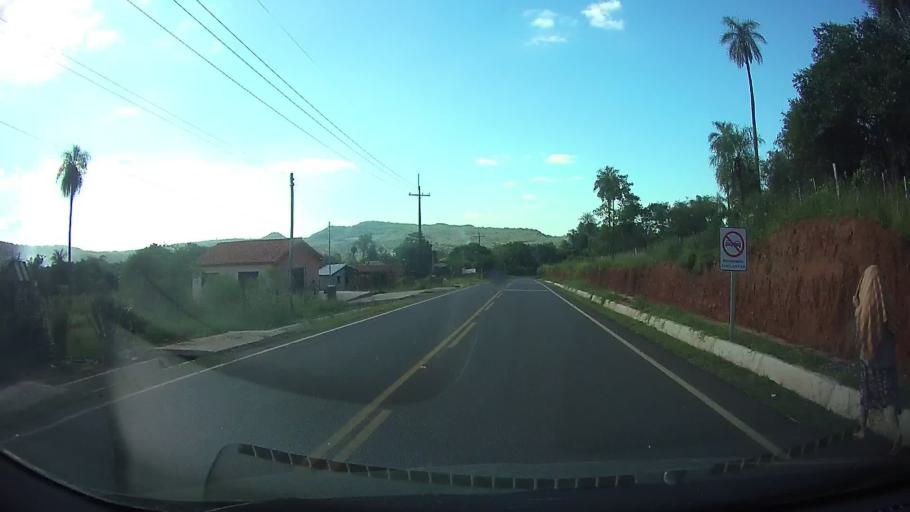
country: PY
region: Cordillera
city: Caacupe
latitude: -25.3645
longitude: -57.1460
